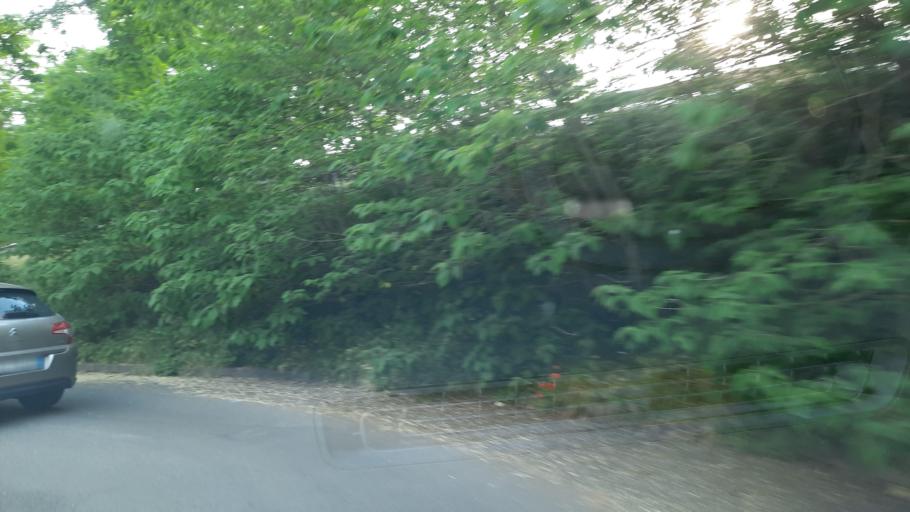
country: IT
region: Lombardy
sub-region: Provincia di Pavia
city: Pavia
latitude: 45.1926
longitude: 9.1526
